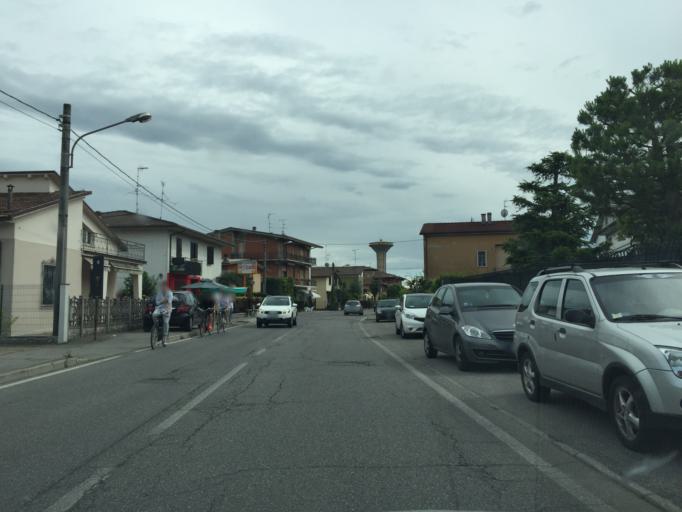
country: IT
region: Lombardy
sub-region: Provincia di Brescia
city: Ghedi
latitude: 45.4109
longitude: 10.2765
